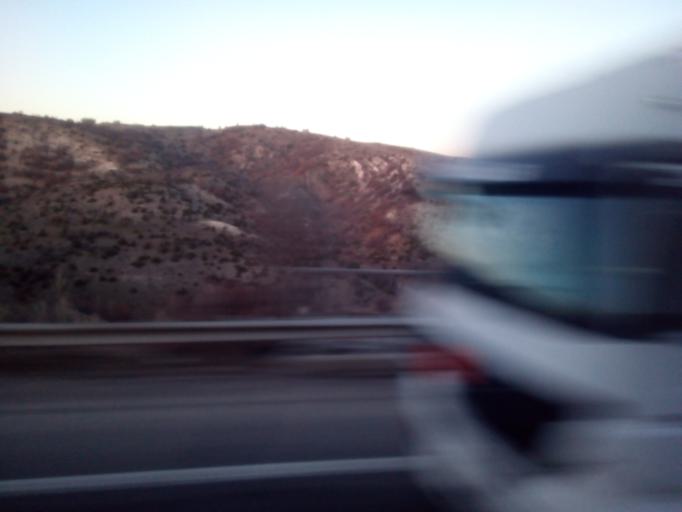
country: TR
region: Ankara
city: Kazan
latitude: 40.2039
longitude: 32.5764
